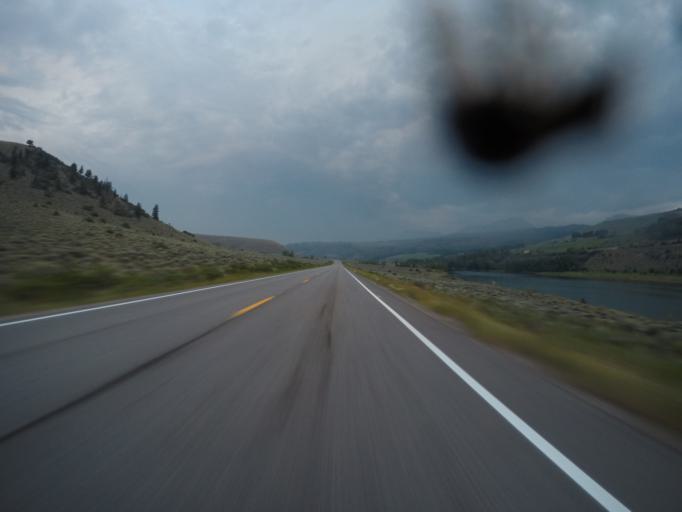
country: US
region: Colorado
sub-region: Eagle County
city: Vail
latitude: 39.8492
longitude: -106.2331
